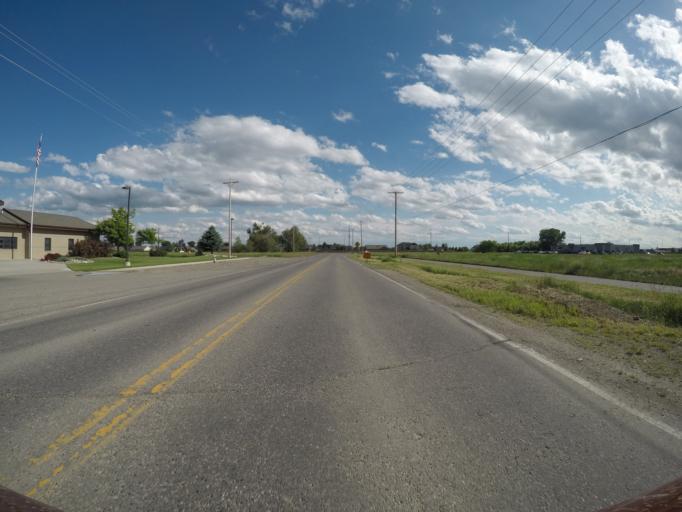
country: US
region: Montana
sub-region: Yellowstone County
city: Billings
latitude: 45.7859
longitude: -108.6527
